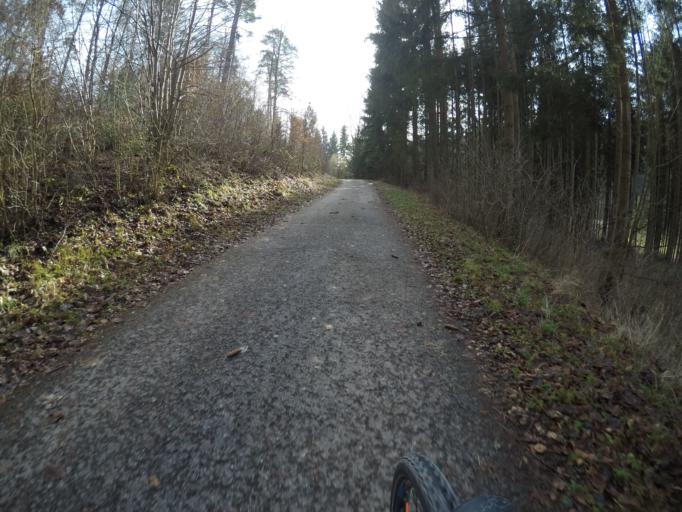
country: DE
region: Baden-Wuerttemberg
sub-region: Regierungsbezirk Stuttgart
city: Oberjettingen
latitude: 48.6072
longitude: 8.7868
